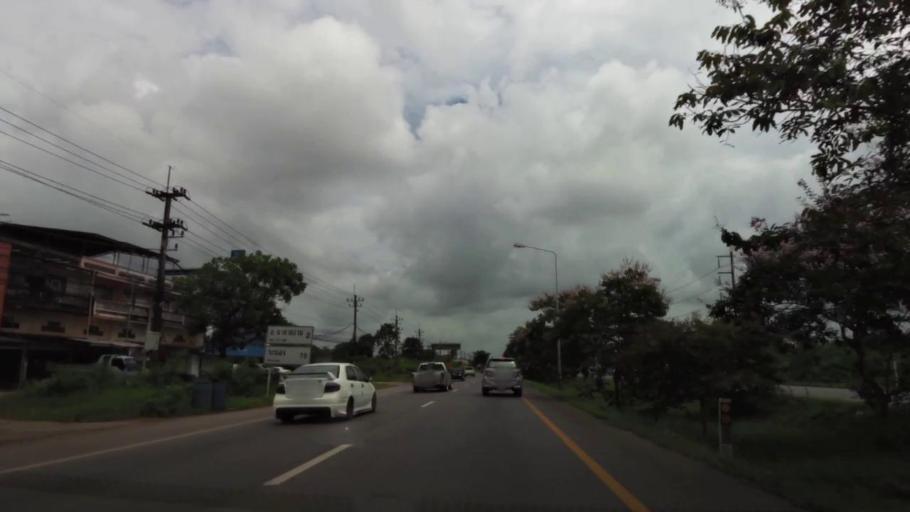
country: TH
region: Chanthaburi
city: Na Yai Am
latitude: 12.7622
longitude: 101.8545
